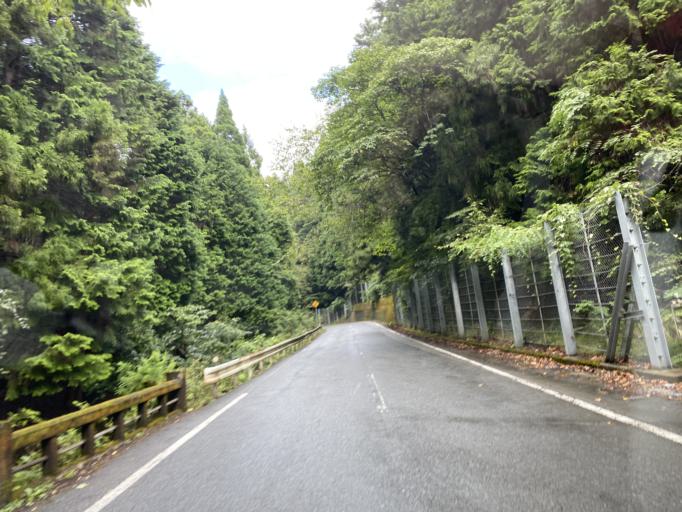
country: JP
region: Kyoto
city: Fukuchiyama
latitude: 35.2980
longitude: 134.9530
